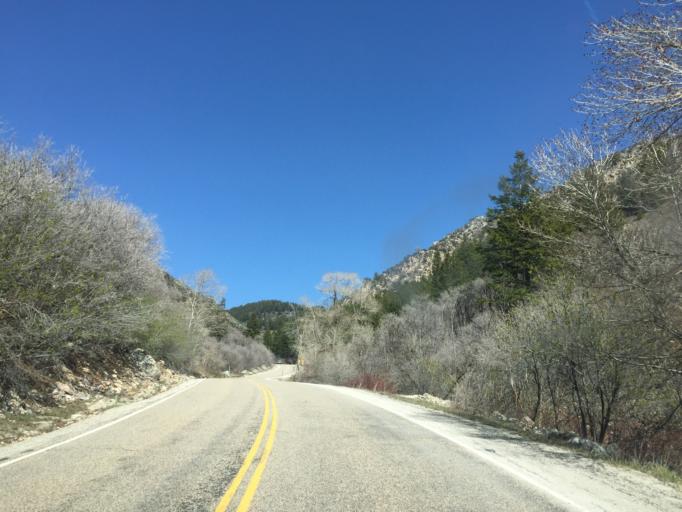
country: US
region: Utah
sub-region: Weber County
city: Wolf Creek
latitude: 41.3522
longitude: -111.8030
